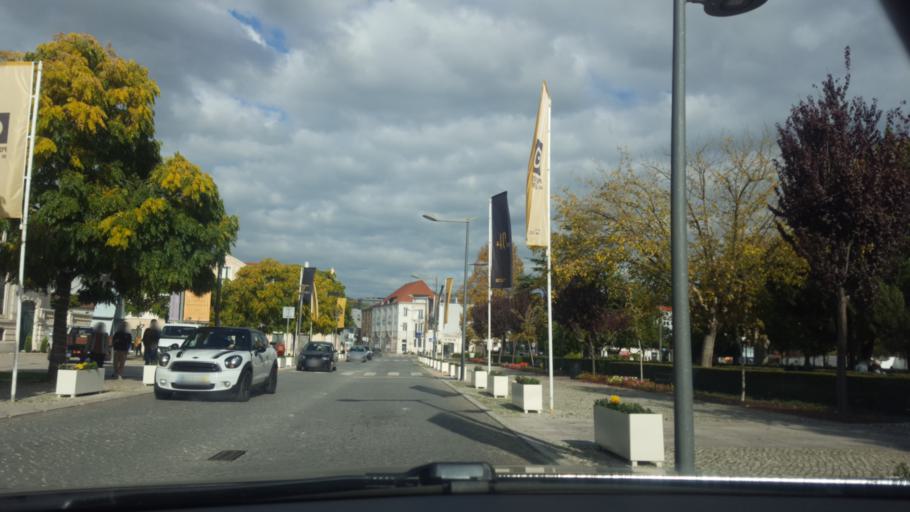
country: PT
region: Leiria
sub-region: Leiria
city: Leiria
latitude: 39.7444
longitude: -8.8071
